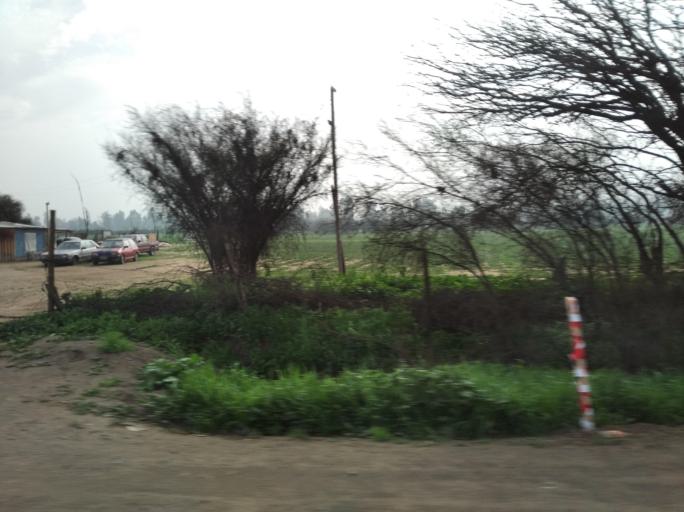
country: CL
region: Santiago Metropolitan
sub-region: Provincia de Chacabuco
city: Lampa
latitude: -33.3136
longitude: -70.8390
